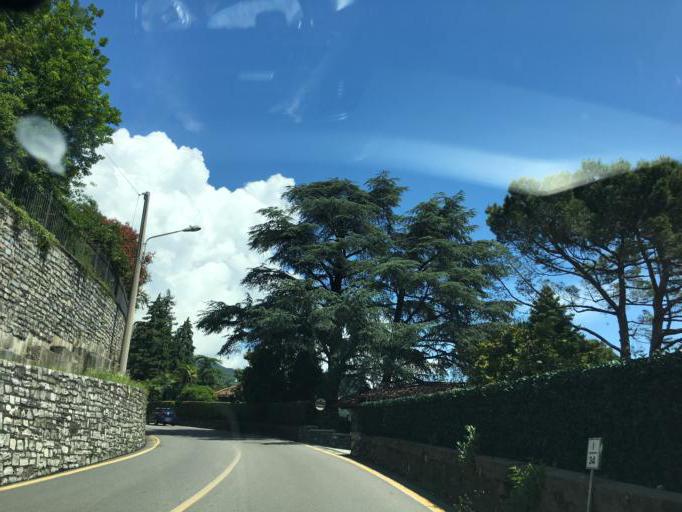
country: IT
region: Lombardy
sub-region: Provincia di Como
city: Menaggio
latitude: 46.0204
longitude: 9.2288
